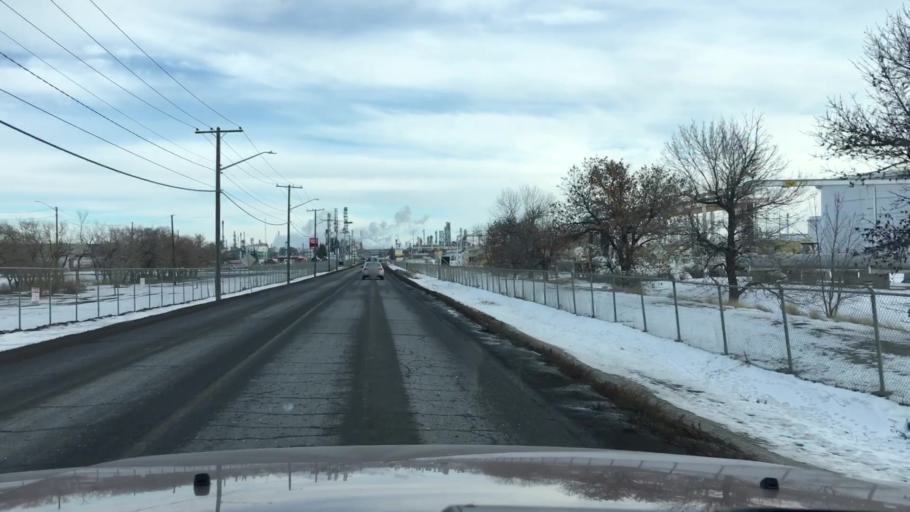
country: CA
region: Saskatchewan
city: Regina
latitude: 50.4843
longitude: -104.5914
